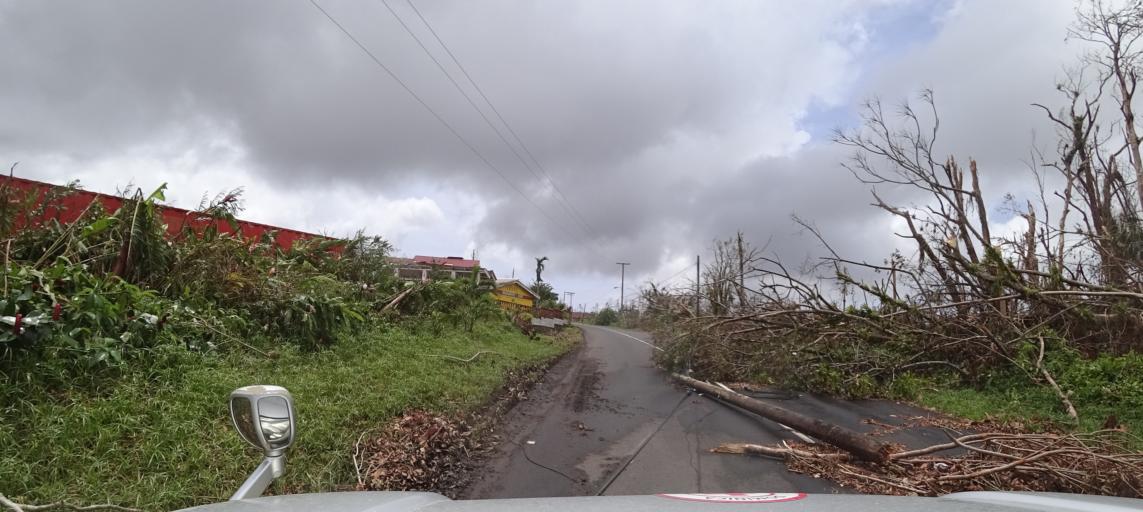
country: DM
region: Saint Paul
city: Pont Casse
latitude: 15.3963
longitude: -61.3440
